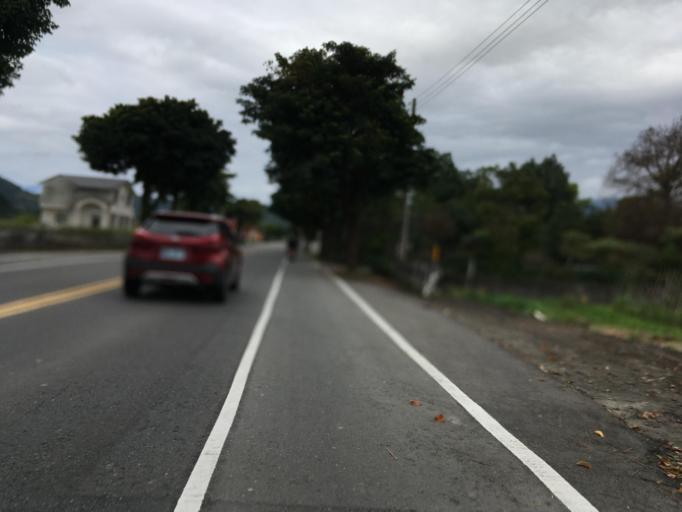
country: TW
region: Taiwan
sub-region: Yilan
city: Yilan
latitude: 24.6633
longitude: 121.6345
